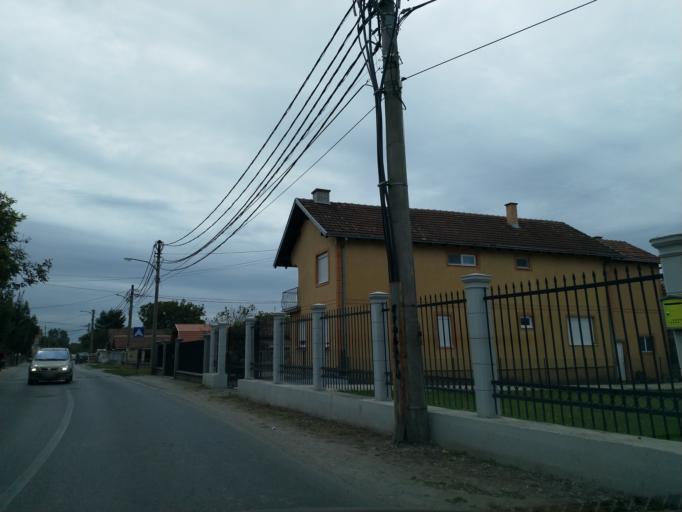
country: RS
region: Central Serbia
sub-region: Pomoravski Okrug
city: Paracin
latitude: 43.8562
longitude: 21.3977
